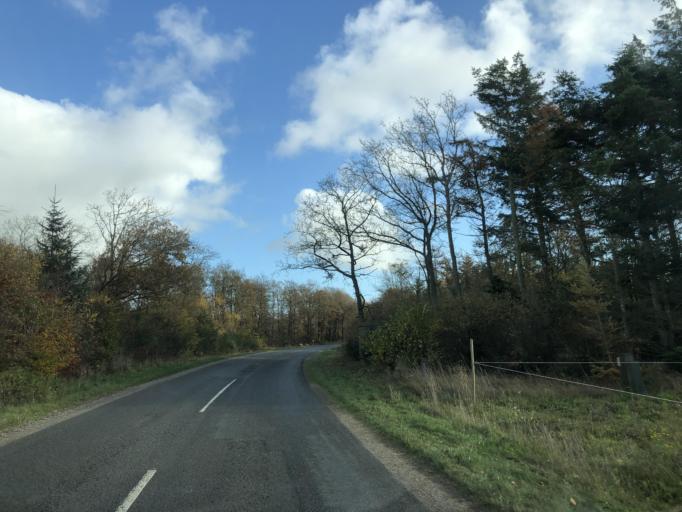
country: DK
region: Central Jutland
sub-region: Ringkobing-Skjern Kommune
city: Ringkobing
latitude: 56.1394
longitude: 8.3221
